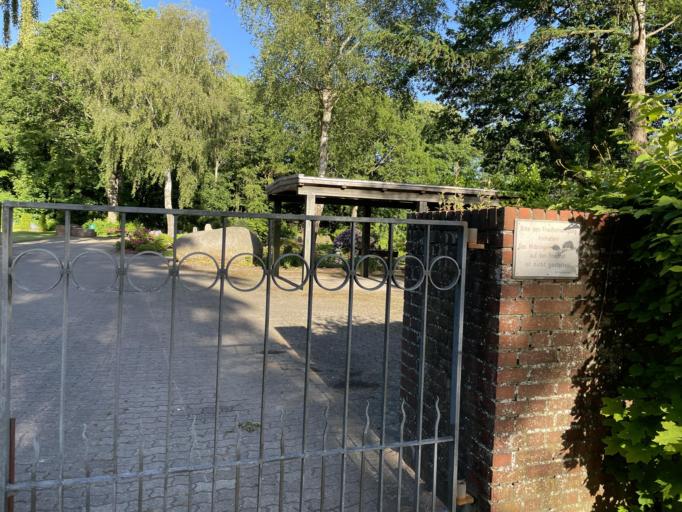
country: DE
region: Schleswig-Holstein
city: Mildstedt
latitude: 54.4621
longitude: 9.0985
